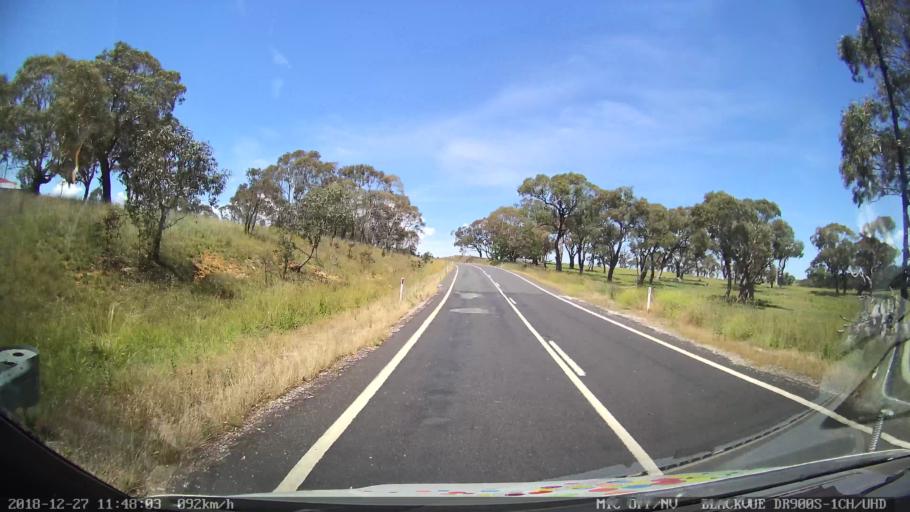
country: AU
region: New South Wales
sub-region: Bathurst Regional
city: Perthville
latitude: -33.6017
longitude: 149.4381
